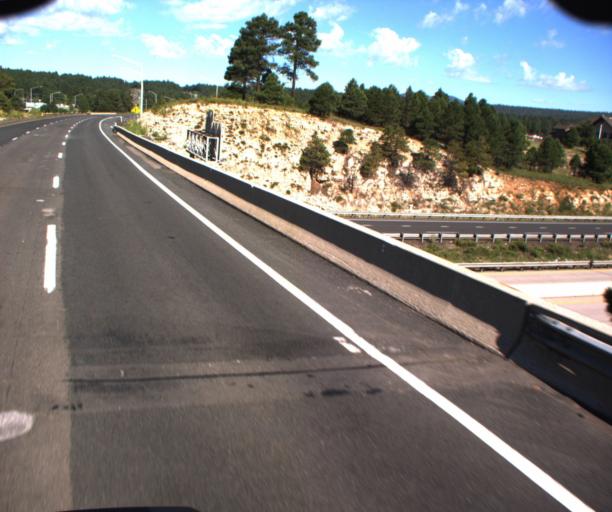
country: US
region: Arizona
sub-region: Coconino County
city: Flagstaff
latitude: 35.1721
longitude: -111.6616
